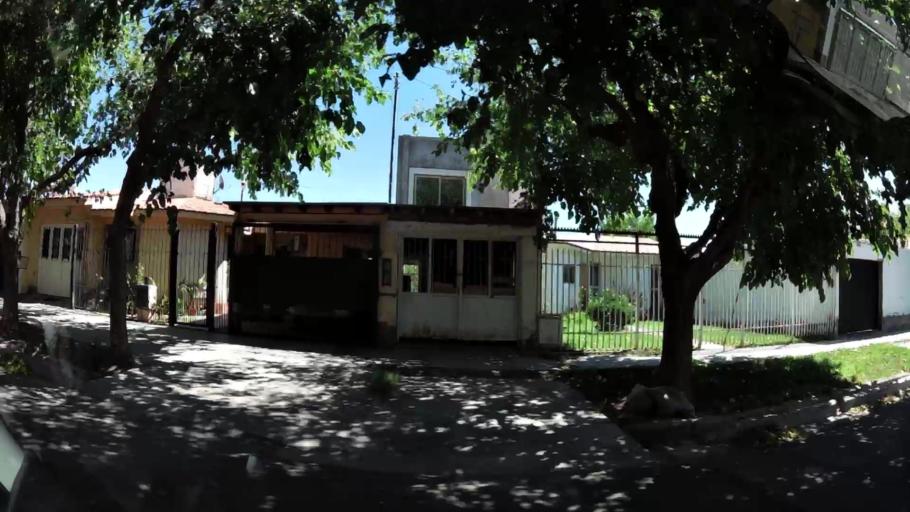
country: AR
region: Mendoza
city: Las Heras
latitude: -32.8509
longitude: -68.8507
